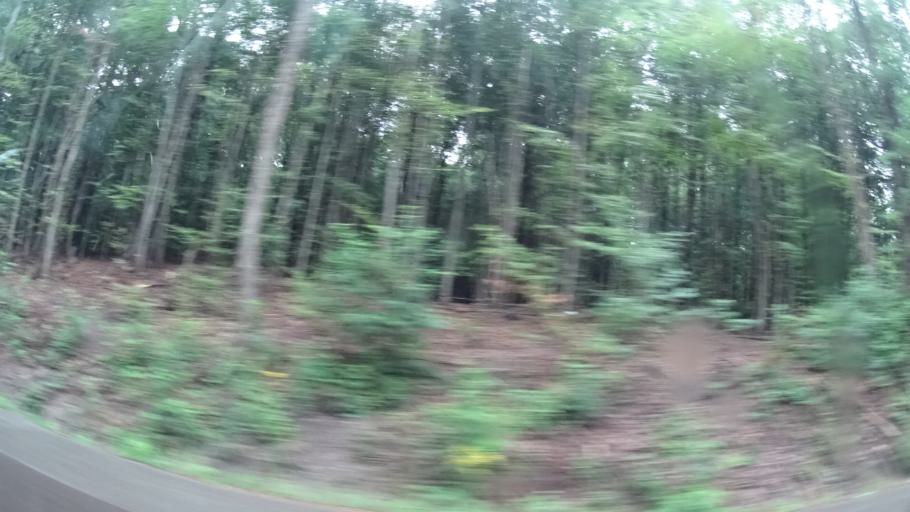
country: DE
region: Saarland
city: Quierschied
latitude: 49.3240
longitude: 7.0635
